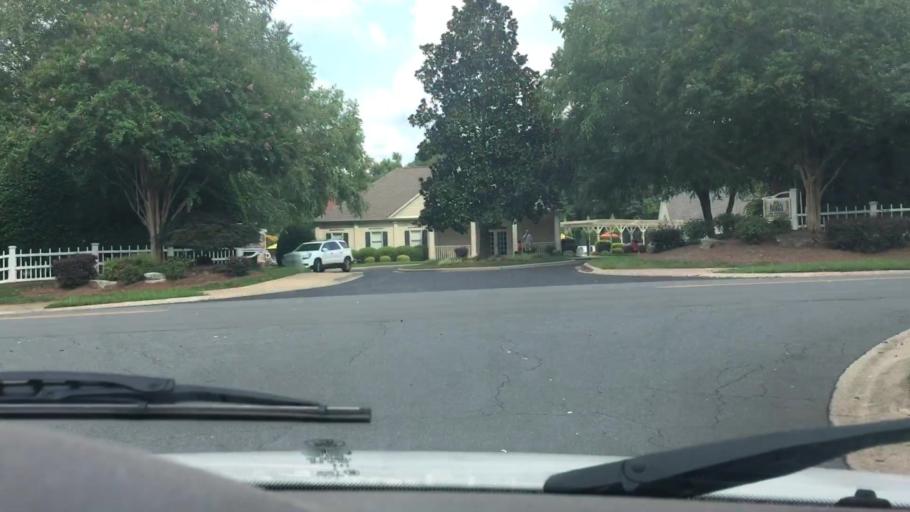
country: US
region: North Carolina
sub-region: Mecklenburg County
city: Huntersville
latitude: 35.4231
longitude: -80.8831
